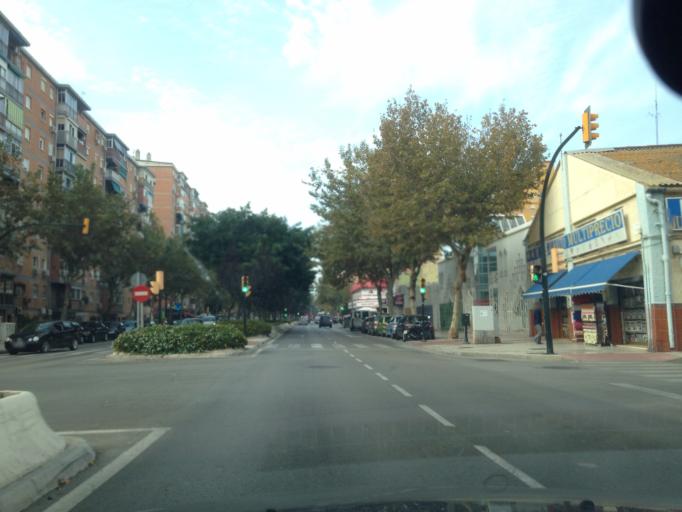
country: ES
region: Andalusia
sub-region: Provincia de Malaga
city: Malaga
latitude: 36.6997
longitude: -4.4531
